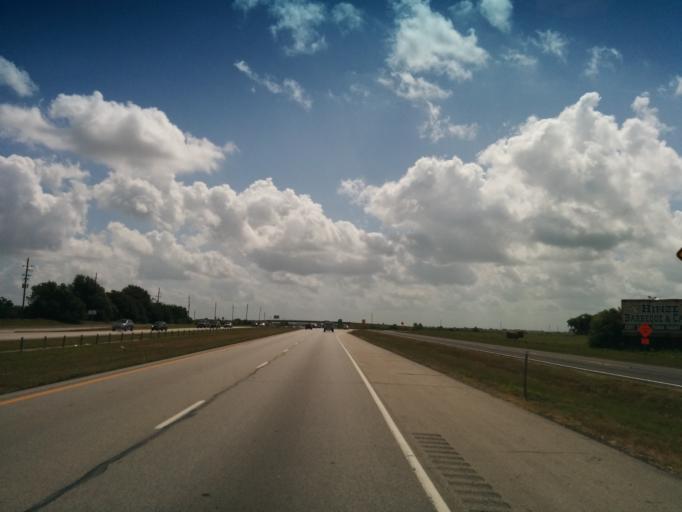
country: US
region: Texas
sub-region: Austin County
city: Sealy
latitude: 29.7576
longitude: -96.2261
